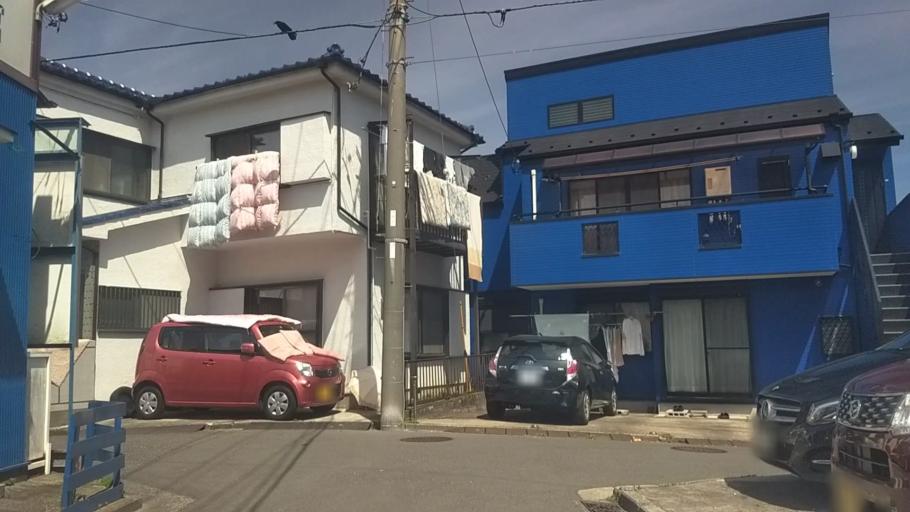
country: JP
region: Kanagawa
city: Yokohama
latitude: 35.4324
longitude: 139.6291
